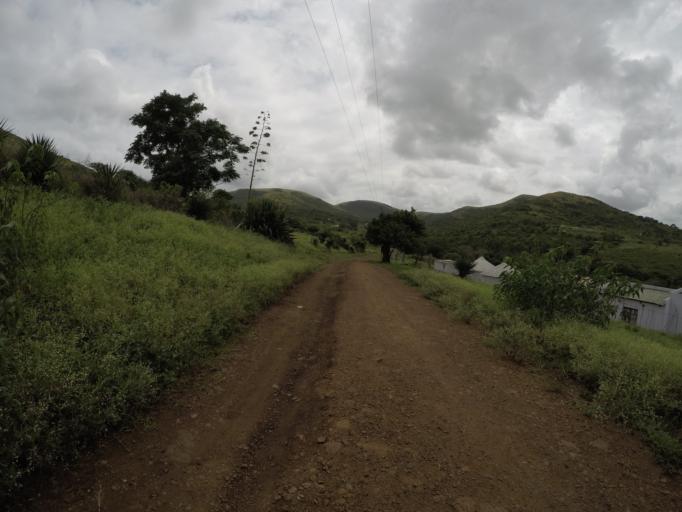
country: ZA
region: KwaZulu-Natal
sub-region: uThungulu District Municipality
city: Empangeni
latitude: -28.5874
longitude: 31.8887
